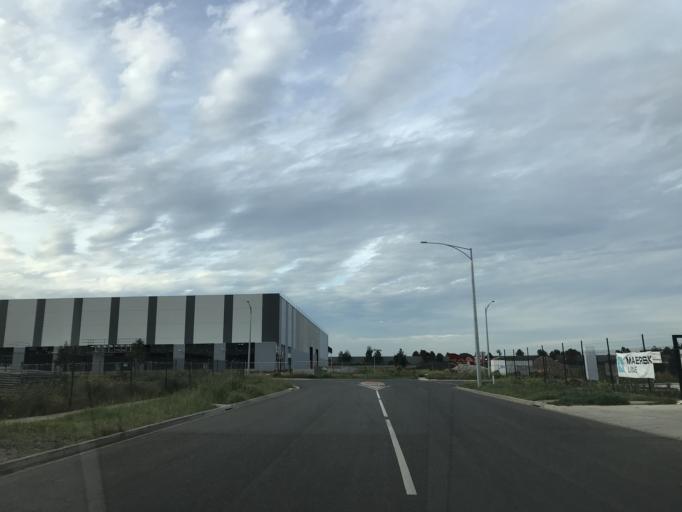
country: AU
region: Victoria
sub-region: Brimbank
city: Derrimut
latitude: -37.8008
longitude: 144.7634
